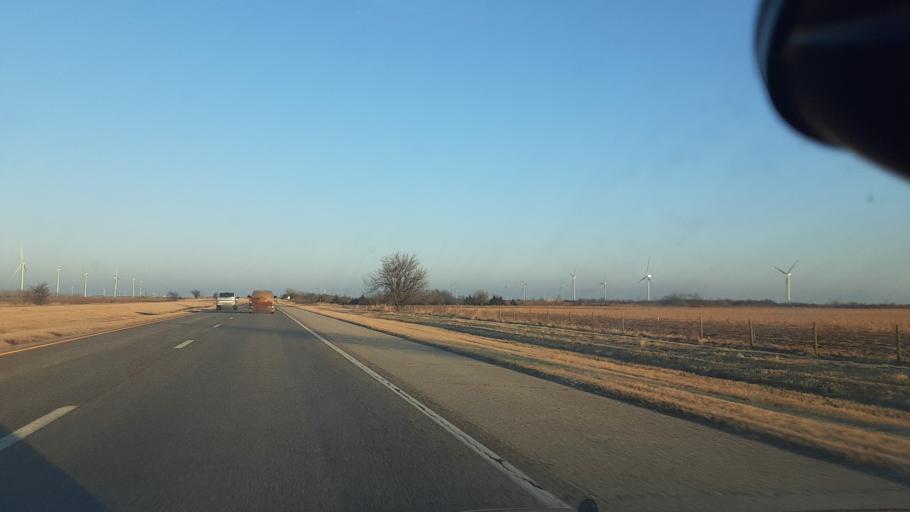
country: US
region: Oklahoma
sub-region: Noble County
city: Perry
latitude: 36.3974
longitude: -97.5267
